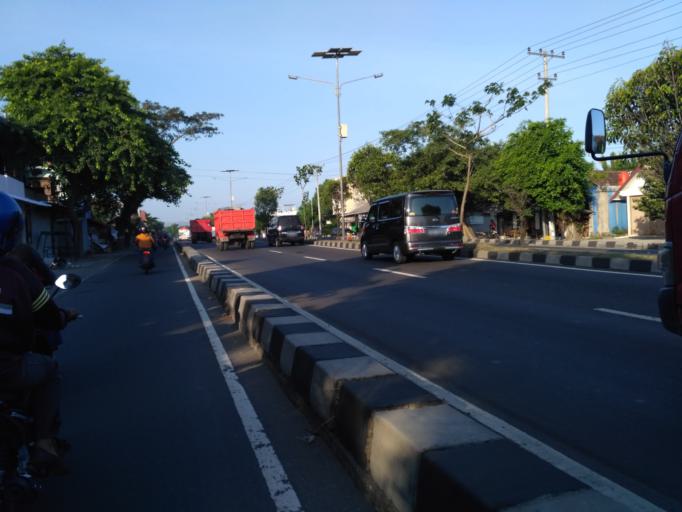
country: ID
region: Daerah Istimewa Yogyakarta
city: Sewon
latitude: -7.8358
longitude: 110.3794
